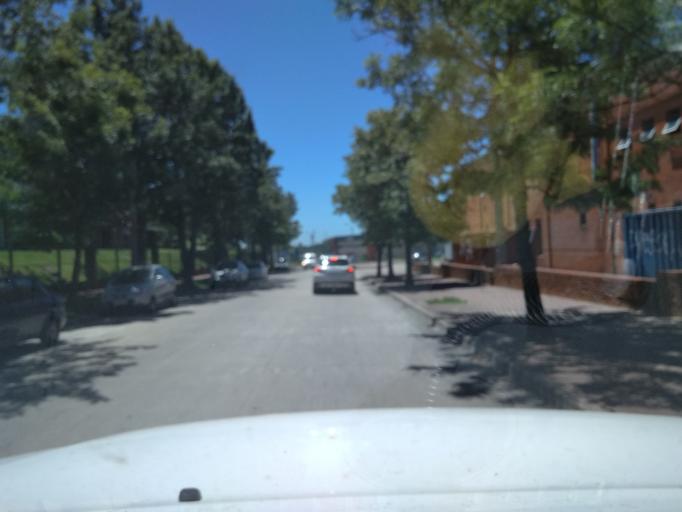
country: UY
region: Canelones
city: Paso de Carrasco
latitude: -34.8802
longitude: -56.0813
